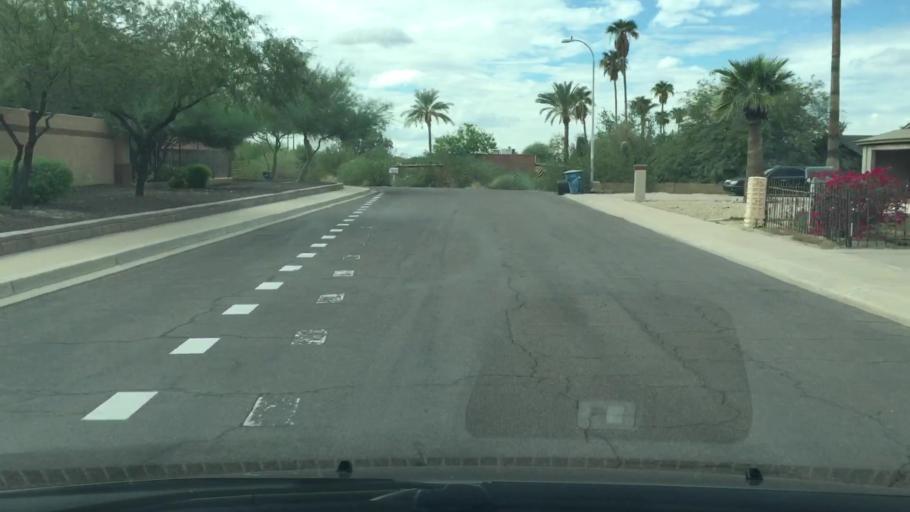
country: US
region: Arizona
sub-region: Maricopa County
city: Guadalupe
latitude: 33.3669
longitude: -112.0432
